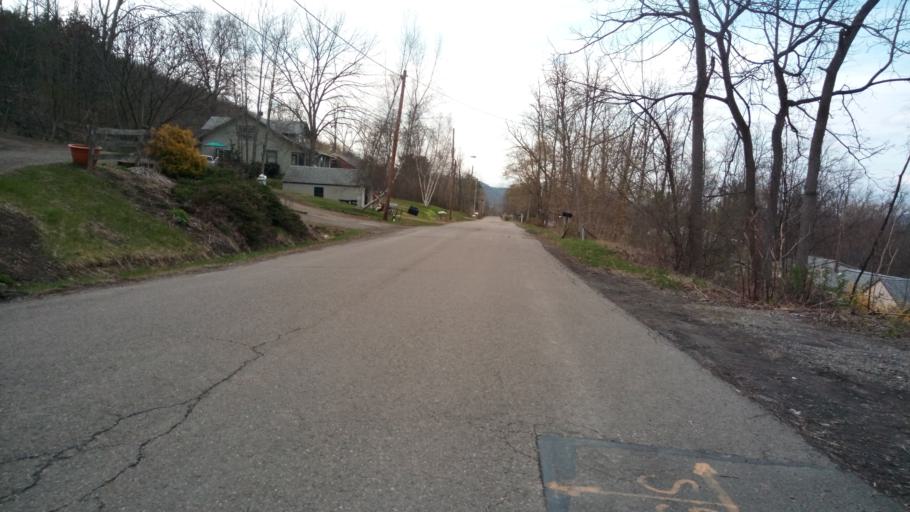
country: US
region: New York
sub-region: Chemung County
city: Southport
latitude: 42.0647
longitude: -76.8209
